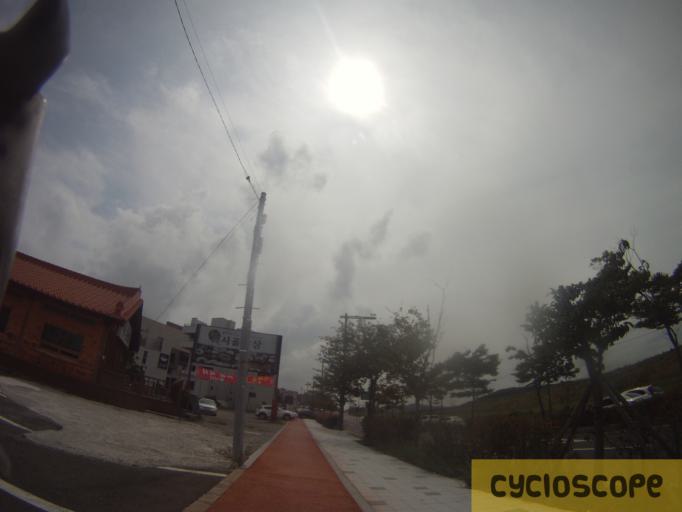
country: KR
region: Busan
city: Kijang
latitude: 35.1948
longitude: 129.2213
